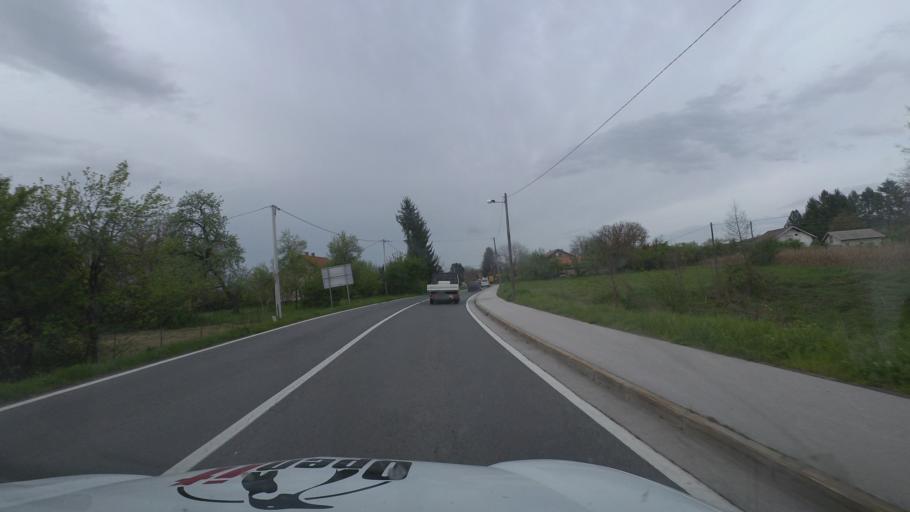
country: HR
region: Karlovacka
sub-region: Grad Karlovac
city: Karlovac
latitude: 45.4248
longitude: 15.6061
